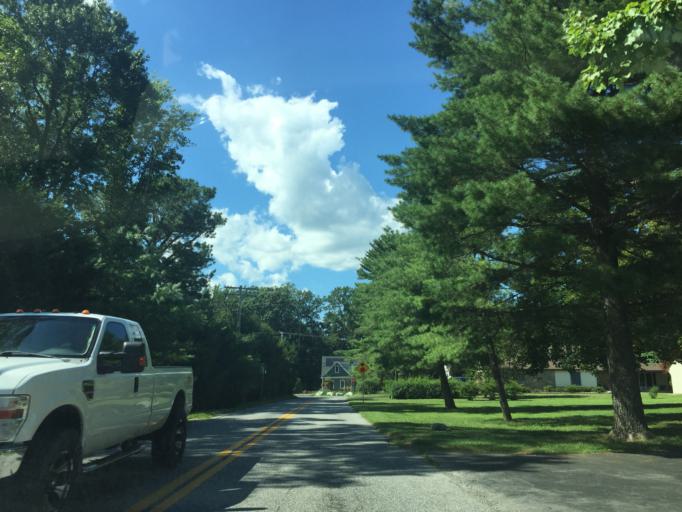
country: US
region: Maryland
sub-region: Baltimore County
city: White Marsh
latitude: 39.4136
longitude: -76.4182
